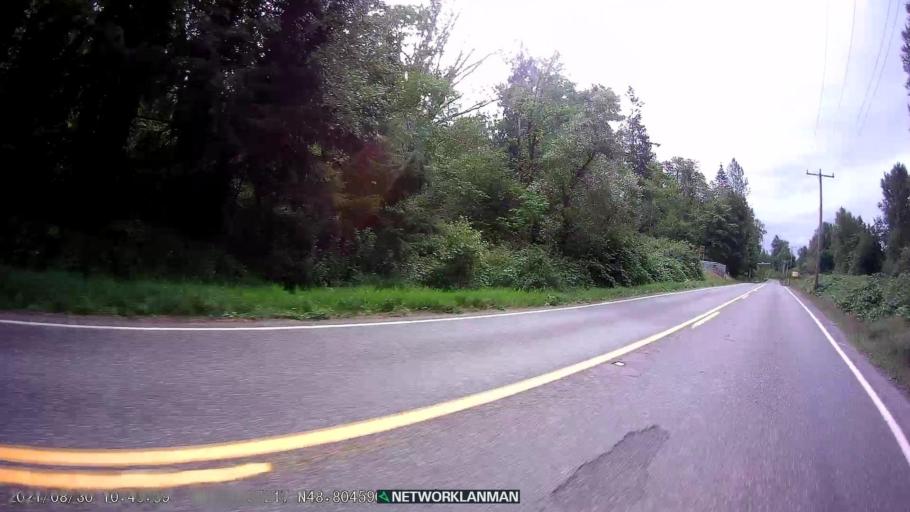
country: US
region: Washington
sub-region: Whatcom County
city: Peaceful Valley
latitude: 48.8043
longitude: -122.1971
